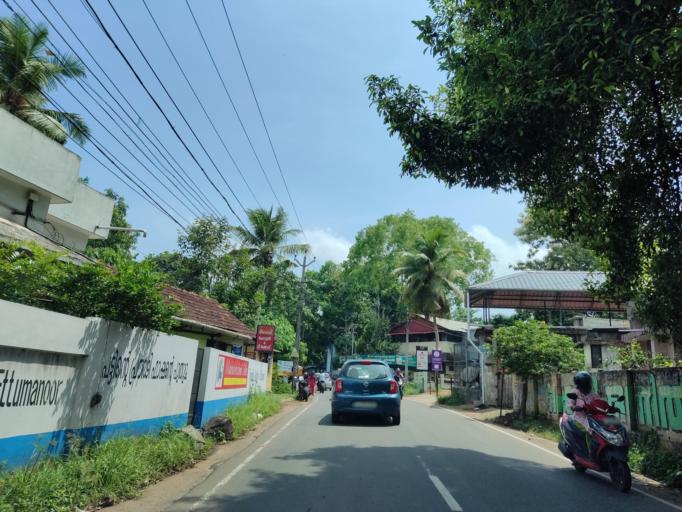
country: IN
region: Kerala
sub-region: Alappuzha
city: Chengannur
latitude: 9.3044
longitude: 76.5883
